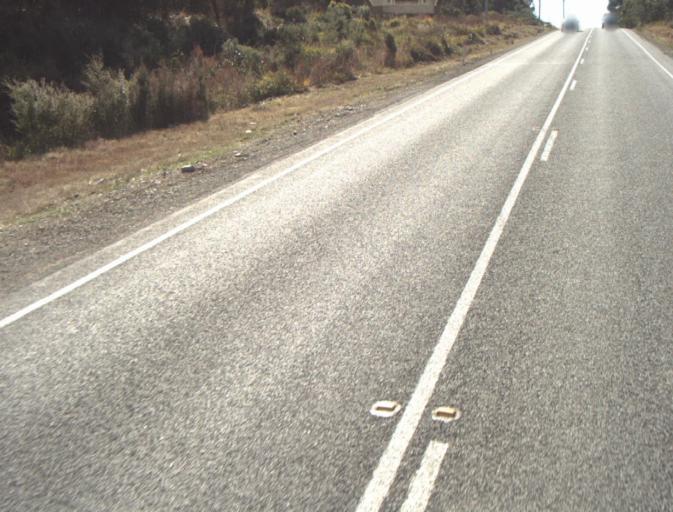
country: AU
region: Tasmania
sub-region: Launceston
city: Mayfield
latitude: -41.3496
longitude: 147.1426
